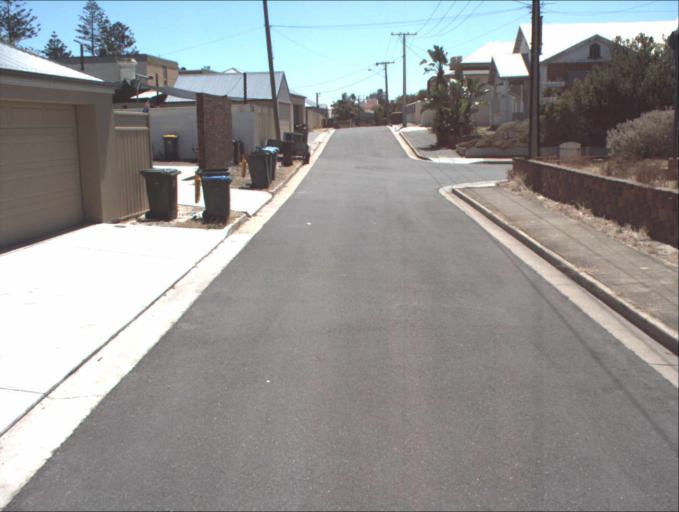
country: AU
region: South Australia
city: Port Adelaide
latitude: -34.8431
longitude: 138.4794
